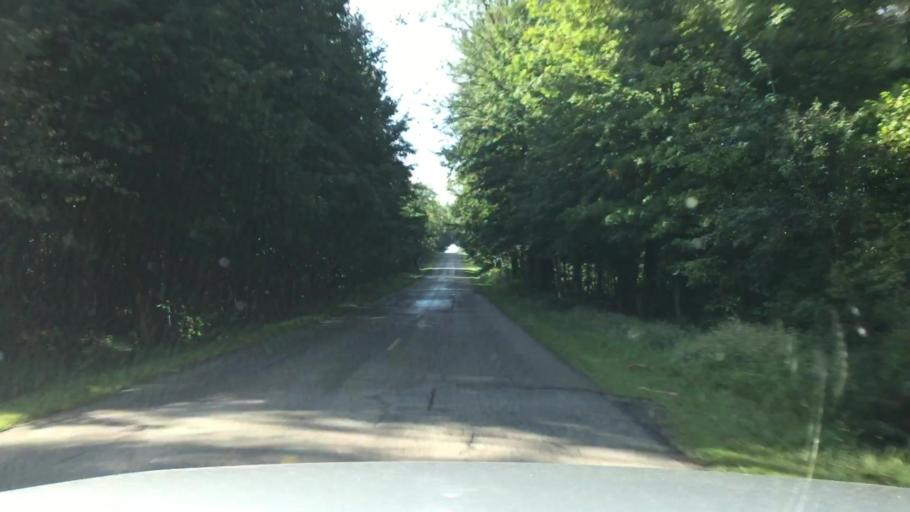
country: US
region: Michigan
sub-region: Lenawee County
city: Hudson
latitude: 41.9246
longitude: -84.4205
